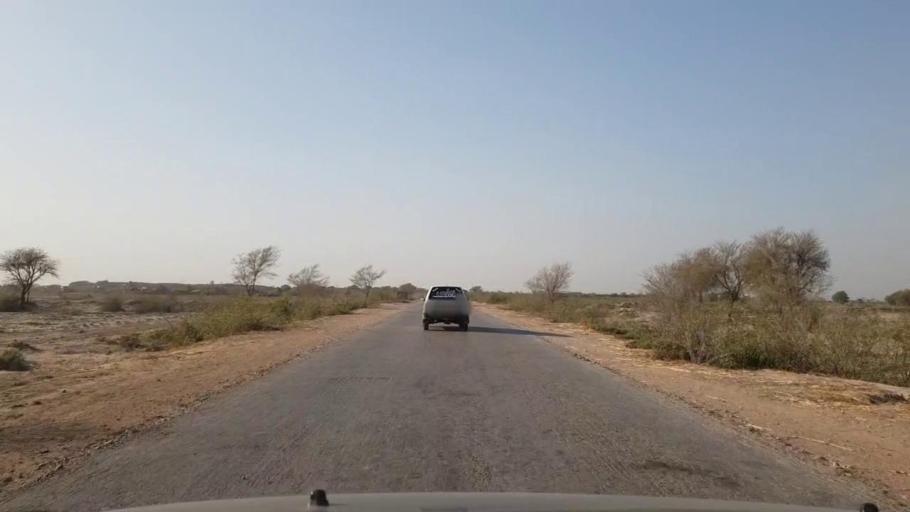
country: PK
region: Sindh
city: Tando Ghulam Ali
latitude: 25.1867
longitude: 68.8140
